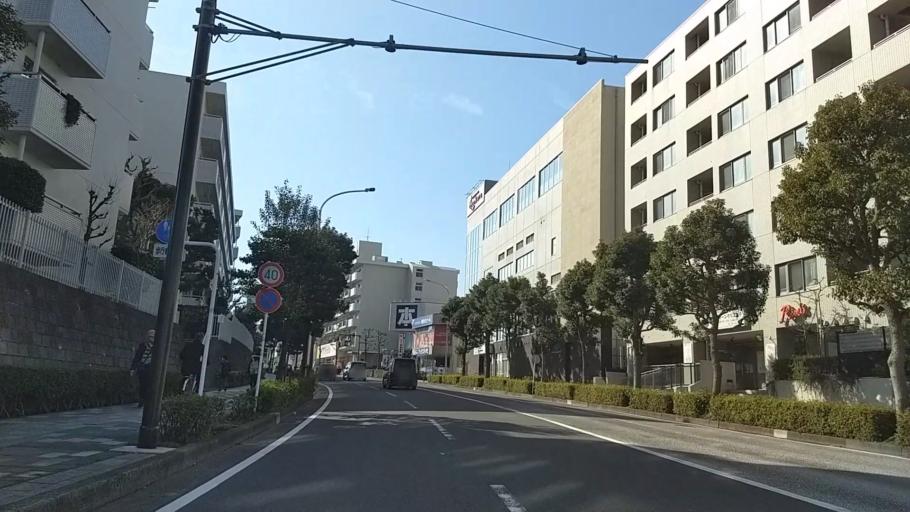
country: JP
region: Kanagawa
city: Kamakura
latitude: 35.3773
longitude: 139.5758
